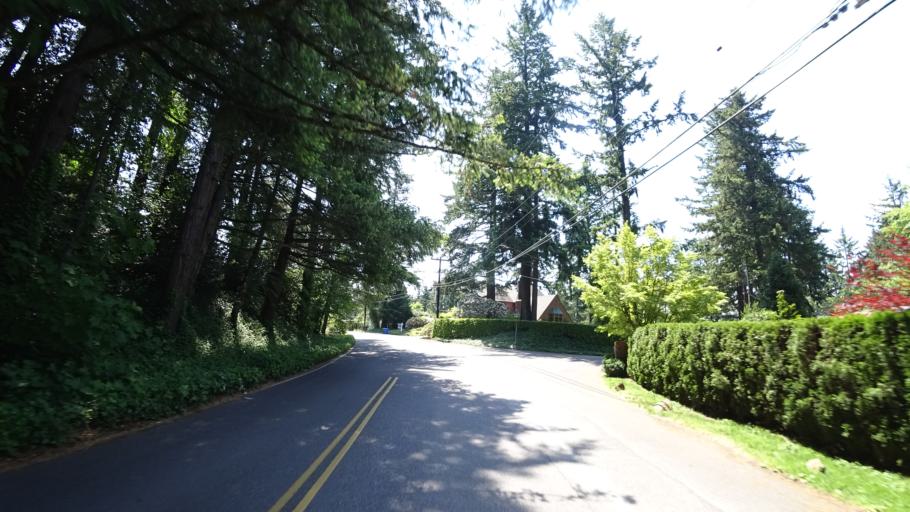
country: US
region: Oregon
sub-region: Washington County
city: West Slope
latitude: 45.5151
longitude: -122.7225
